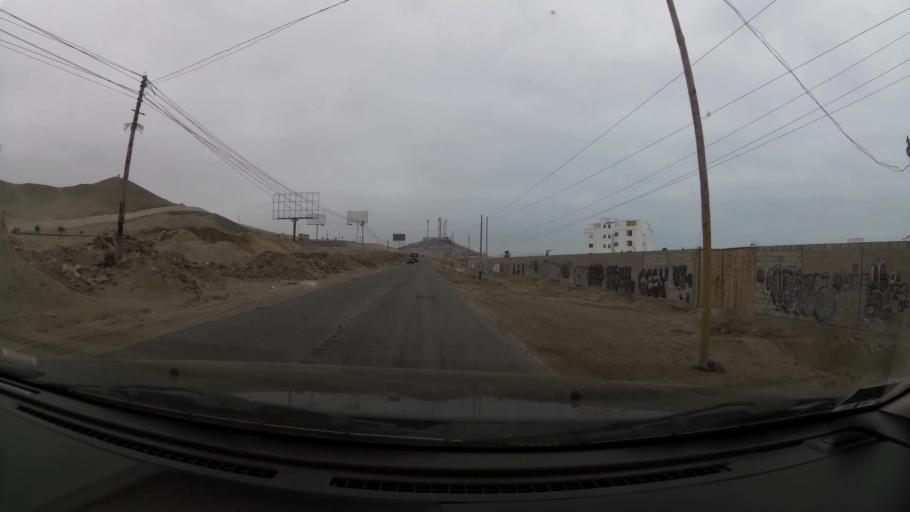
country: PE
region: Lima
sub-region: Lima
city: Punta Hermosa
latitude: -12.3371
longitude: -76.8184
